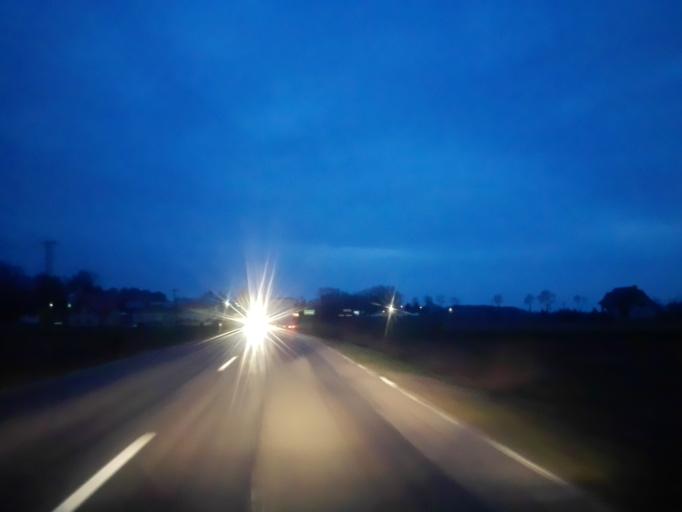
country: PL
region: Podlasie
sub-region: Powiat lomzynski
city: Sniadowo
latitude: 53.0502
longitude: 21.9939
